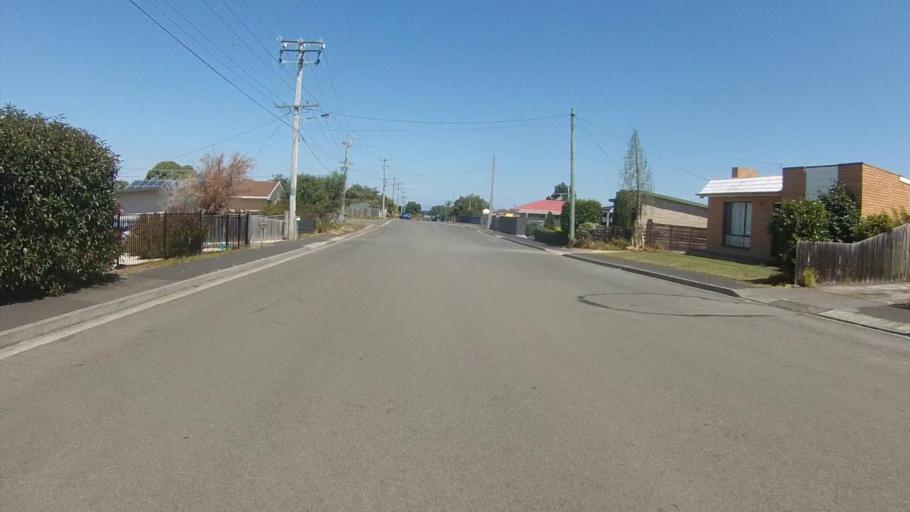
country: AU
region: Tasmania
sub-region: Sorell
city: Sorell
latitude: -42.8007
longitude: 147.5342
